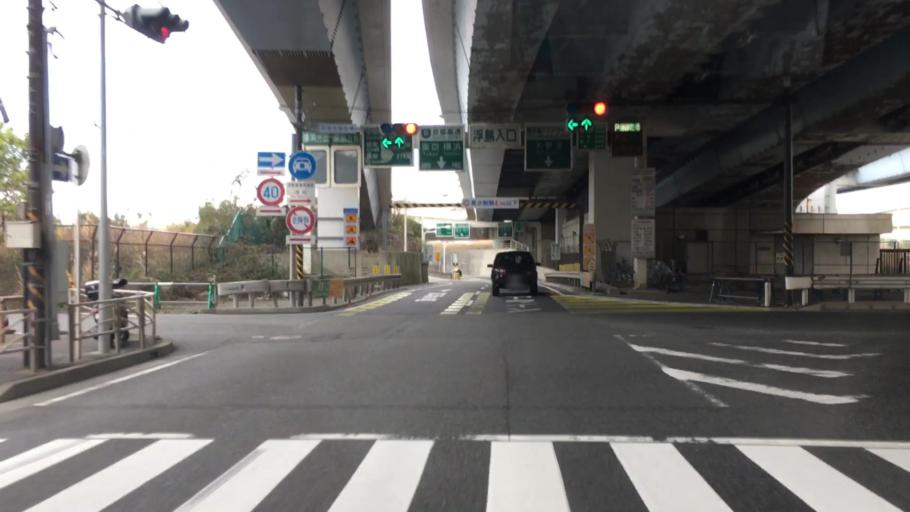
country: JP
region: Kanagawa
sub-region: Kawasaki-shi
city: Kawasaki
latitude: 35.5207
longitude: 139.7877
